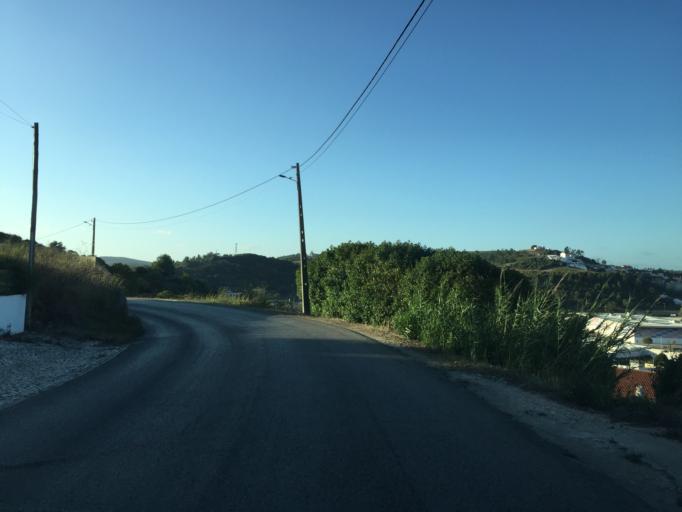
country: PT
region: Lisbon
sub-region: Torres Vedras
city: Torres Vedras
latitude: 39.0897
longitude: -9.2669
